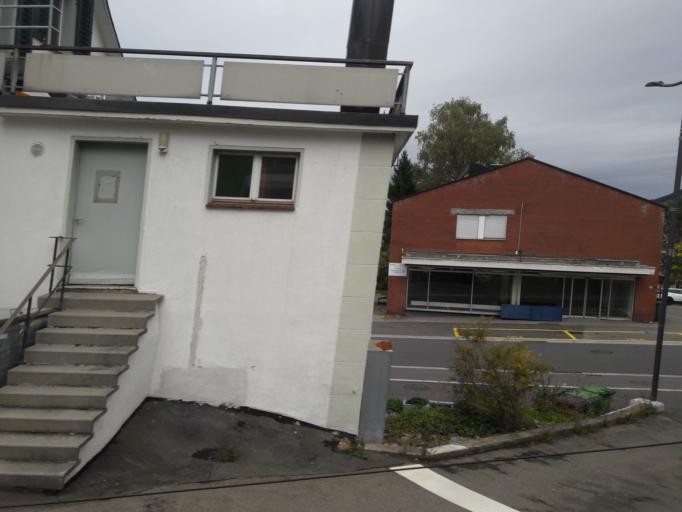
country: CH
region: Schwyz
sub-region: Bezirk Hoefe
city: Schindellegi
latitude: 47.1758
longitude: 8.7101
